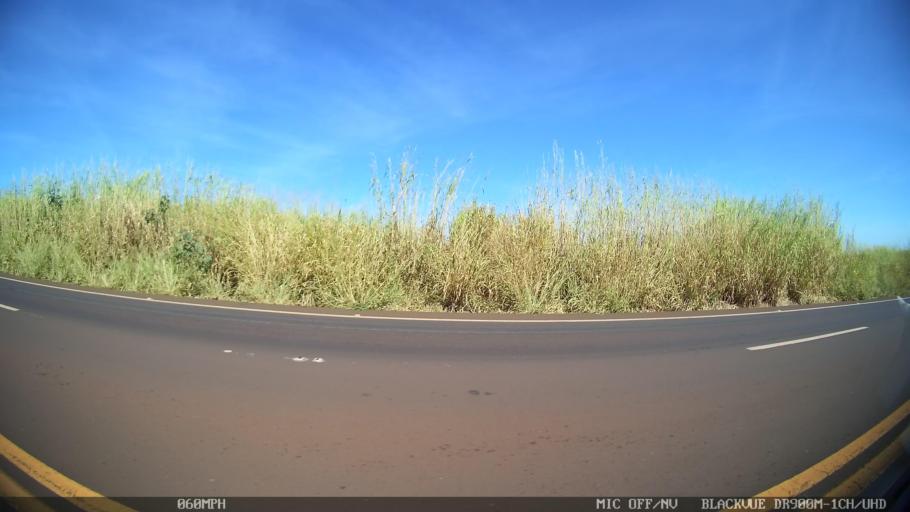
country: BR
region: Sao Paulo
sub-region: Nuporanga
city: Nuporanga
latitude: -20.5595
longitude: -47.6349
